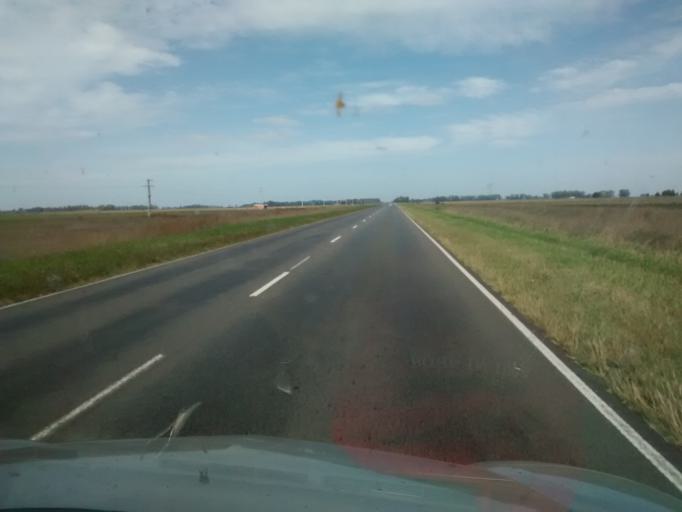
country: AR
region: Buenos Aires
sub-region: Partido de Ayacucho
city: Ayacucho
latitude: -37.0968
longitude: -58.5476
